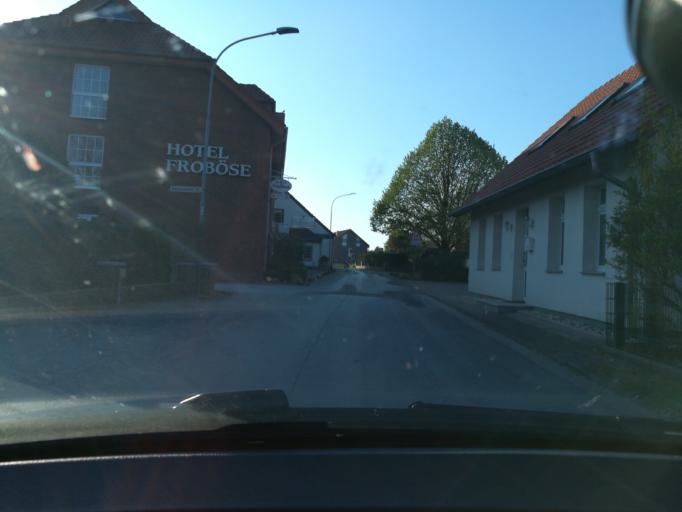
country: DE
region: North Rhine-Westphalia
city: Versmold
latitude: 52.0419
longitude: 8.1530
